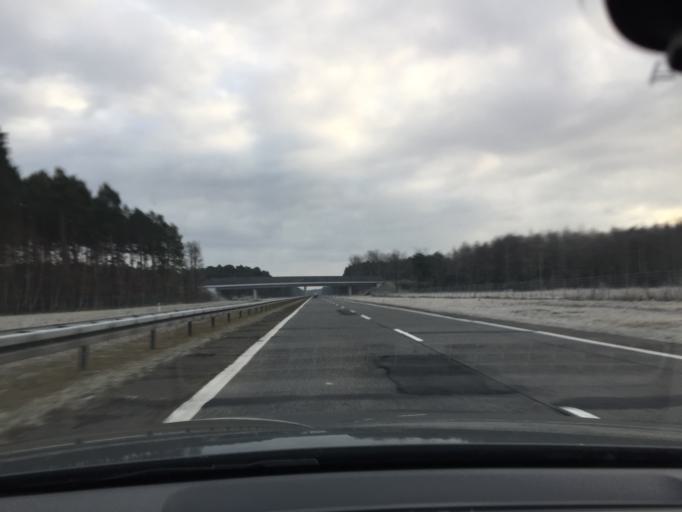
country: PL
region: Lubusz
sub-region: Powiat zarski
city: Trzebiel
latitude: 51.6223
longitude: 14.8961
